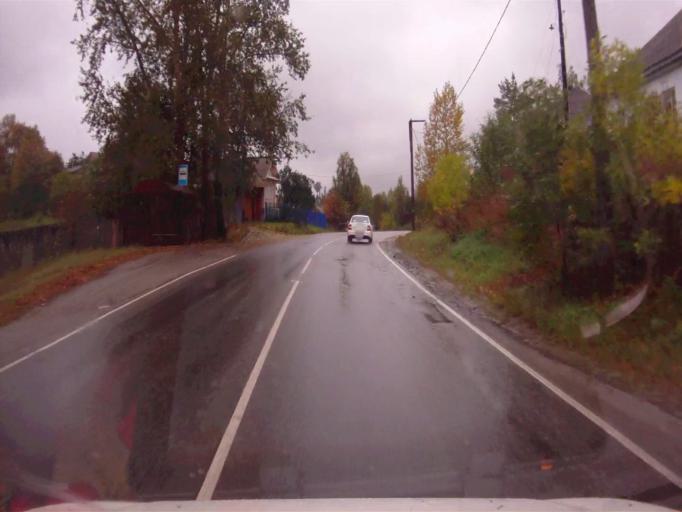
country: RU
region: Chelyabinsk
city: Kyshtym
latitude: 55.7242
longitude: 60.5176
